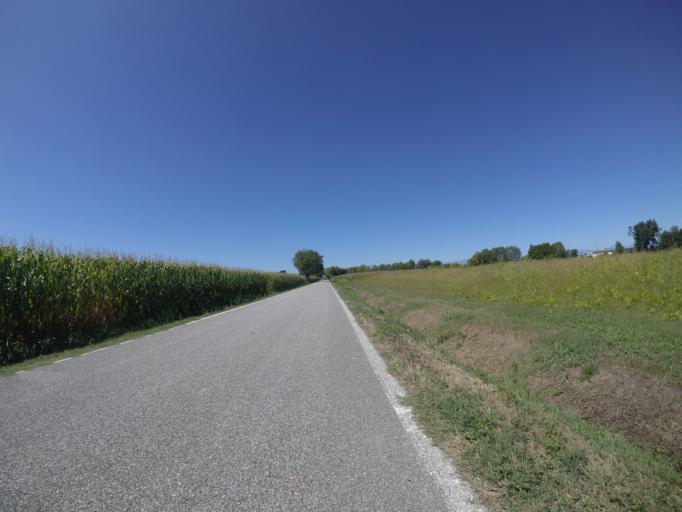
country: IT
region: Friuli Venezia Giulia
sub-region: Provincia di Udine
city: Rivignano
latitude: 45.8584
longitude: 13.0236
